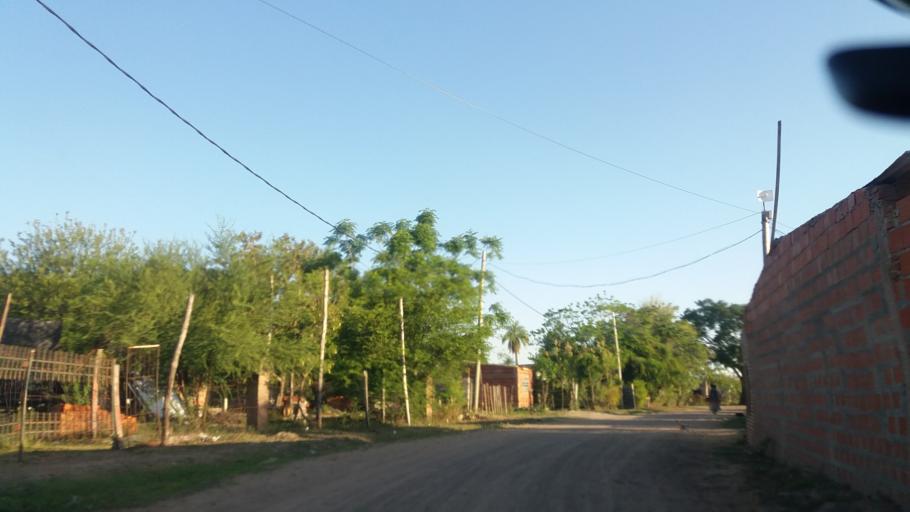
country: AR
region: Corrientes
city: Corrientes
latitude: -27.5195
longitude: -58.8288
